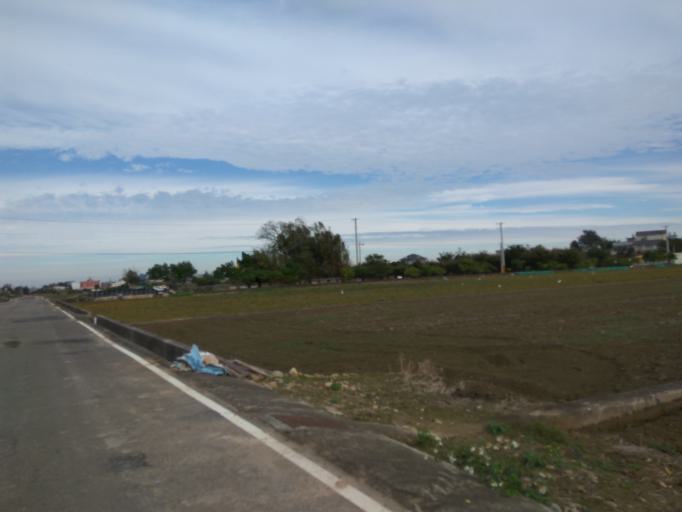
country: TW
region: Taiwan
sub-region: Hsinchu
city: Zhubei
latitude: 24.9521
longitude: 121.1040
